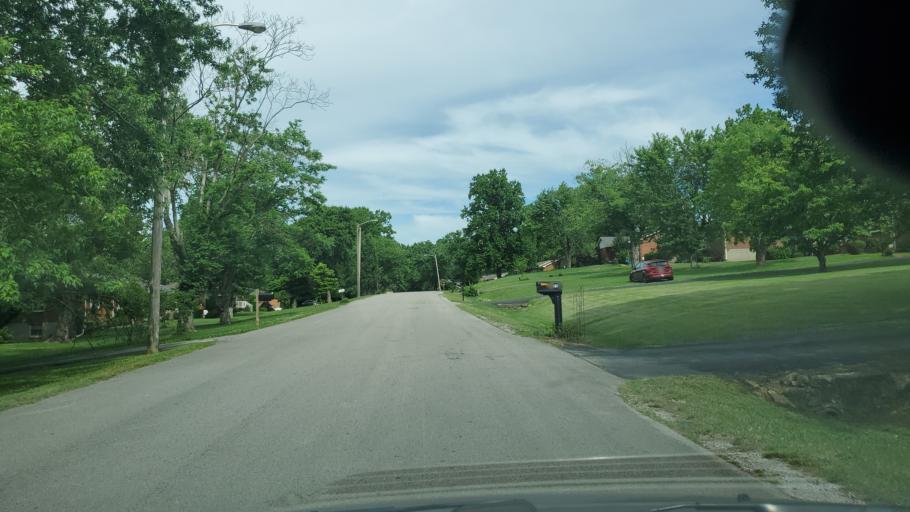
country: US
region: Tennessee
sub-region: Davidson County
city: Lakewood
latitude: 36.2015
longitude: -86.6839
